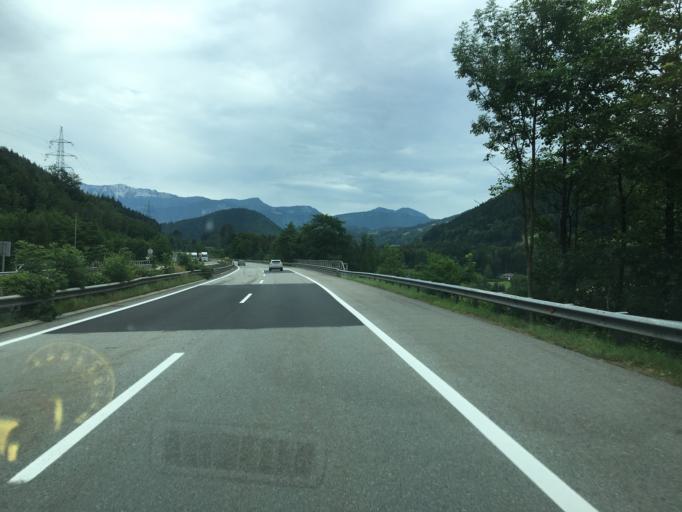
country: AT
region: Styria
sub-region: Politischer Bezirk Liezen
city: Ardning
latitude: 47.6478
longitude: 14.3338
